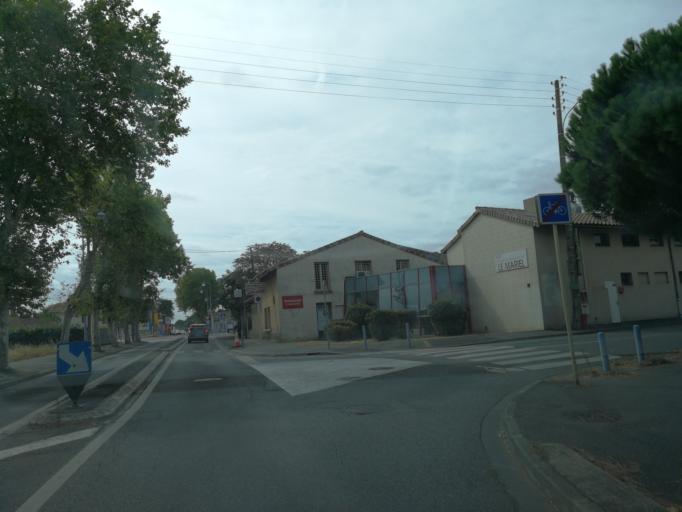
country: FR
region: Midi-Pyrenees
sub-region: Departement de la Haute-Garonne
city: Aucamville
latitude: 43.6797
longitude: 1.4223
